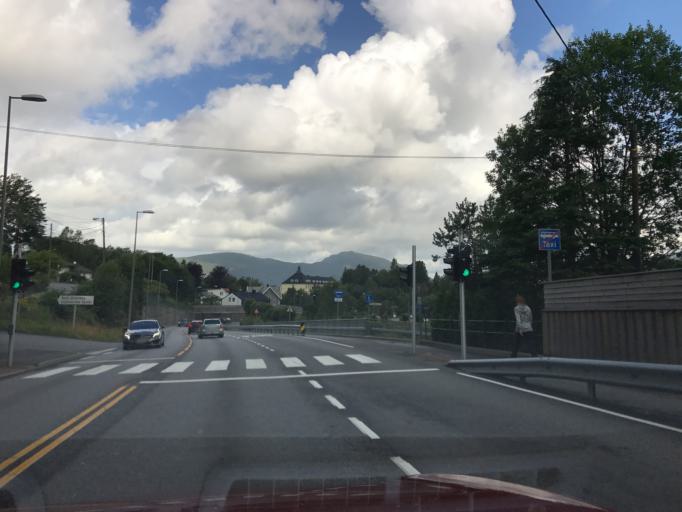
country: NO
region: Hordaland
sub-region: Bergen
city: Sandsli
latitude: 60.3111
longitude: 5.3601
